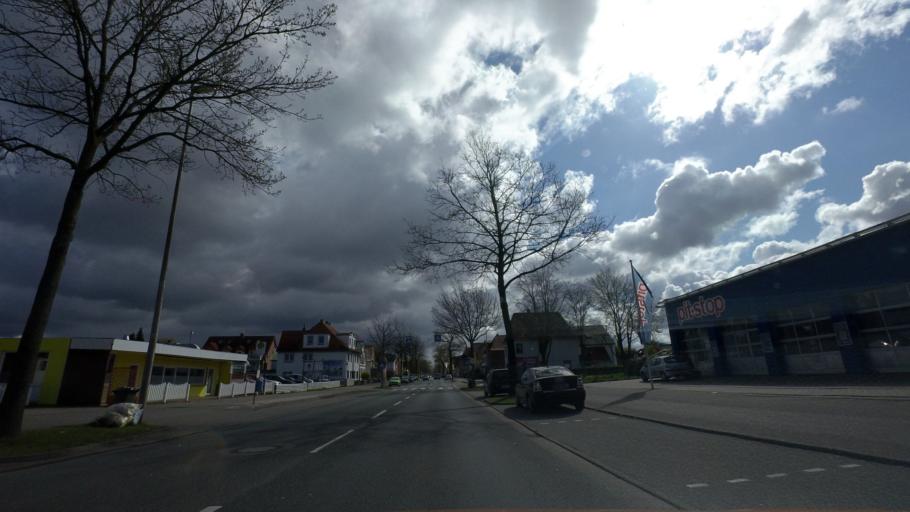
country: DE
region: Lower Saxony
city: Delmenhorst
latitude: 53.0493
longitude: 8.6018
